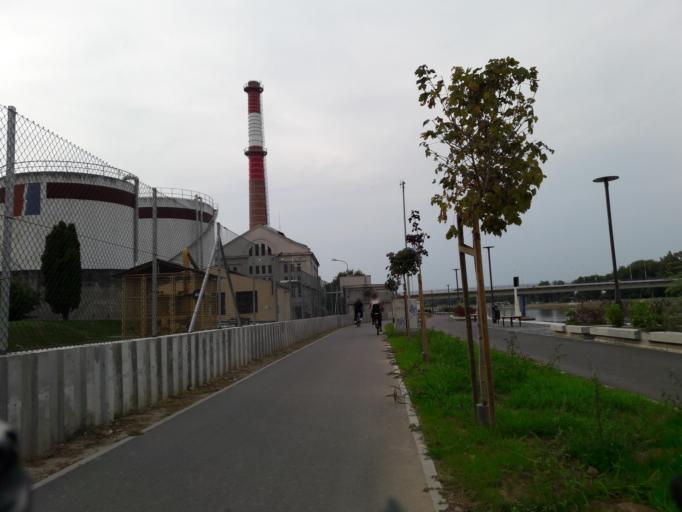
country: HR
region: Osjecko-Baranjska
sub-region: Grad Osijek
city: Osijek
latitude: 45.5602
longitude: 18.7031
